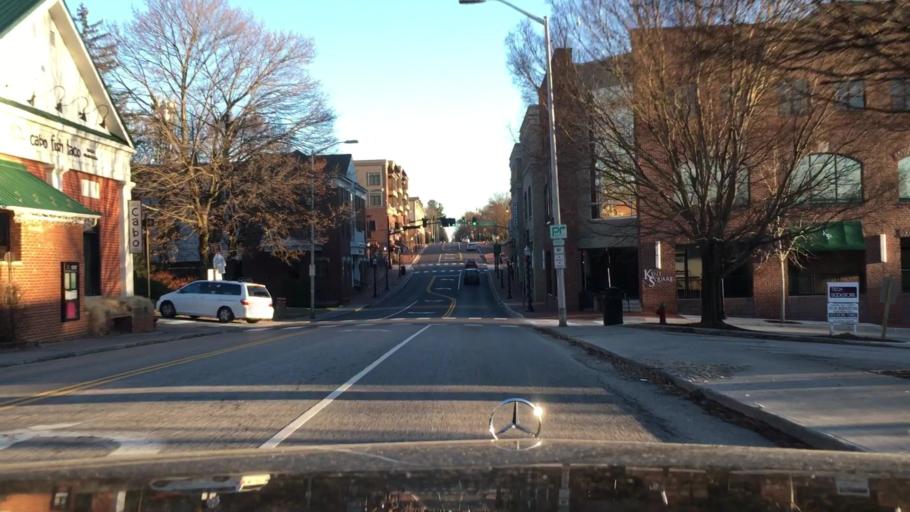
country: US
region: Virginia
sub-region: Montgomery County
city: Blacksburg
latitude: 37.2288
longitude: -80.4135
